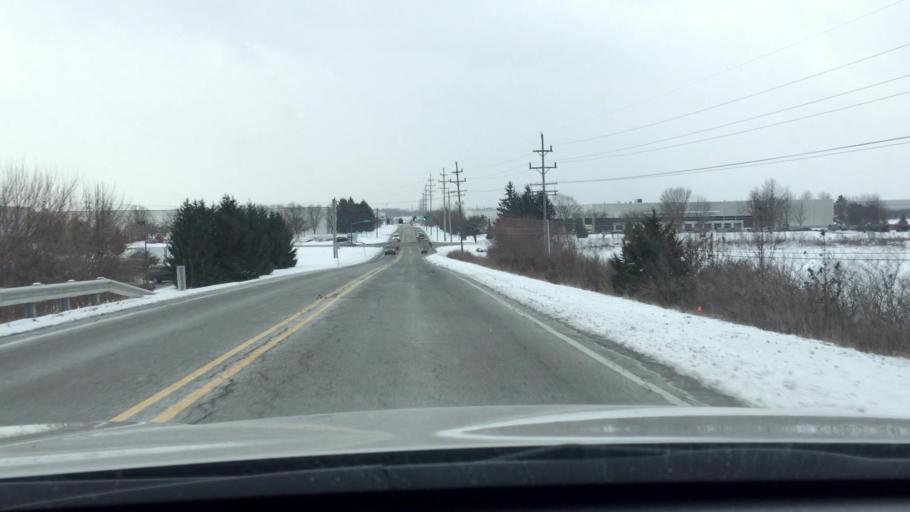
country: US
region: Indiana
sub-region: Hamilton County
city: Fishers
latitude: 39.9665
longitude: -85.9940
